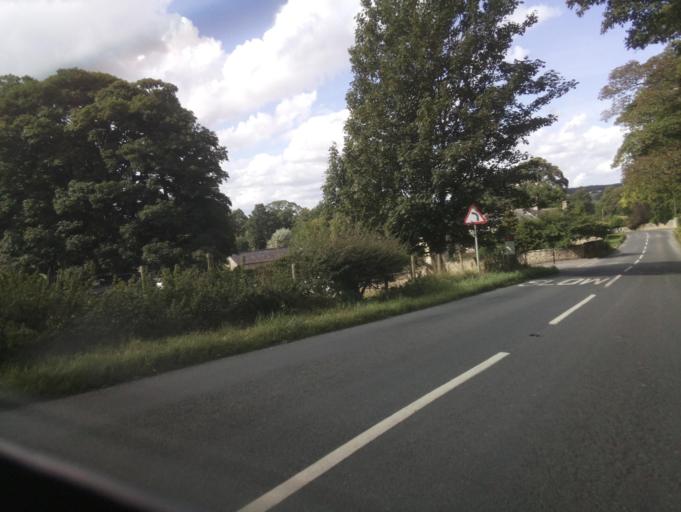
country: GB
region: England
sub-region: North Yorkshire
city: Leyburn
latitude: 54.2662
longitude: -1.7416
